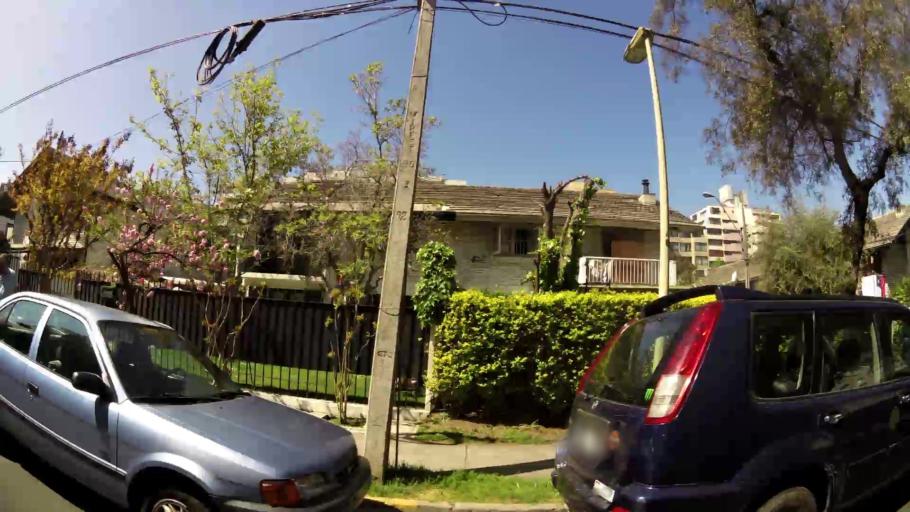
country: CL
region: Santiago Metropolitan
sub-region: Provincia de Santiago
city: Villa Presidente Frei, Nunoa, Santiago, Chile
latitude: -33.4187
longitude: -70.5588
